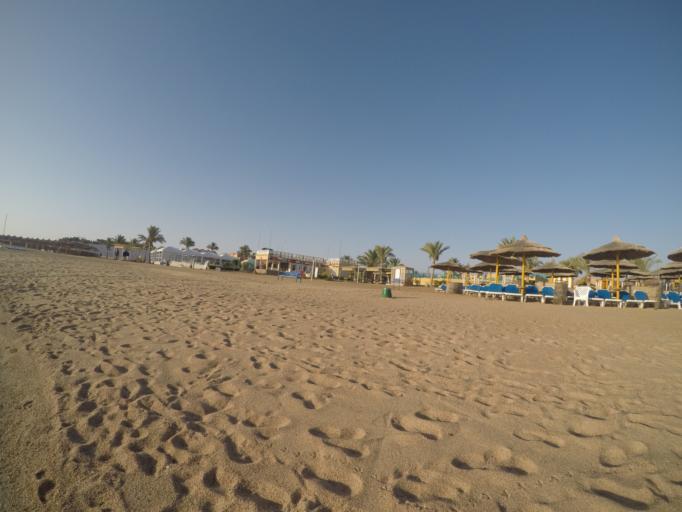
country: EG
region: Red Sea
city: Makadi Bay
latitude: 27.0930
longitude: 33.8515
